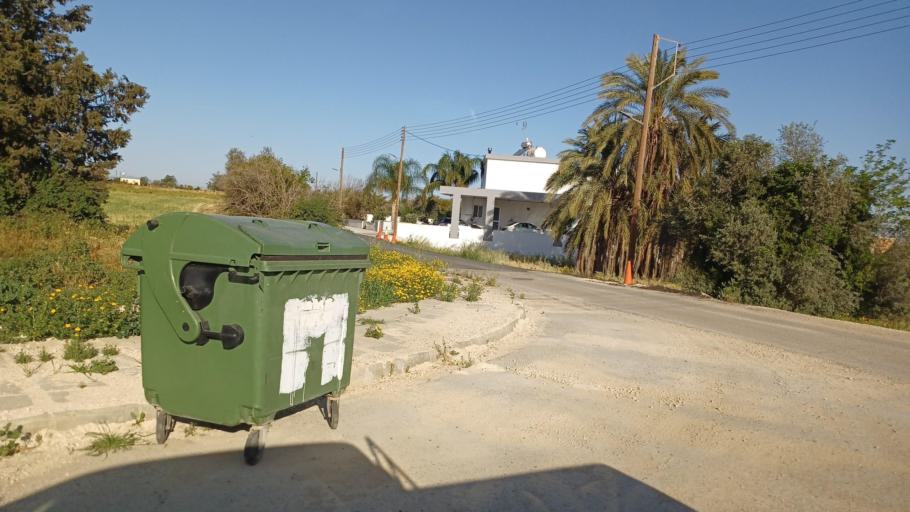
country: CY
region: Lefkosia
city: Kokkinotrimithia
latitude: 35.1507
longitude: 33.1895
